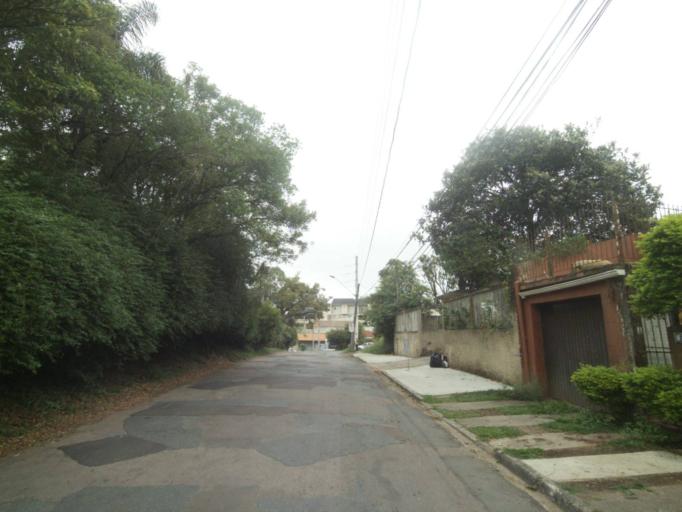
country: BR
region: Parana
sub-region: Curitiba
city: Curitiba
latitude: -25.3865
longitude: -49.2756
